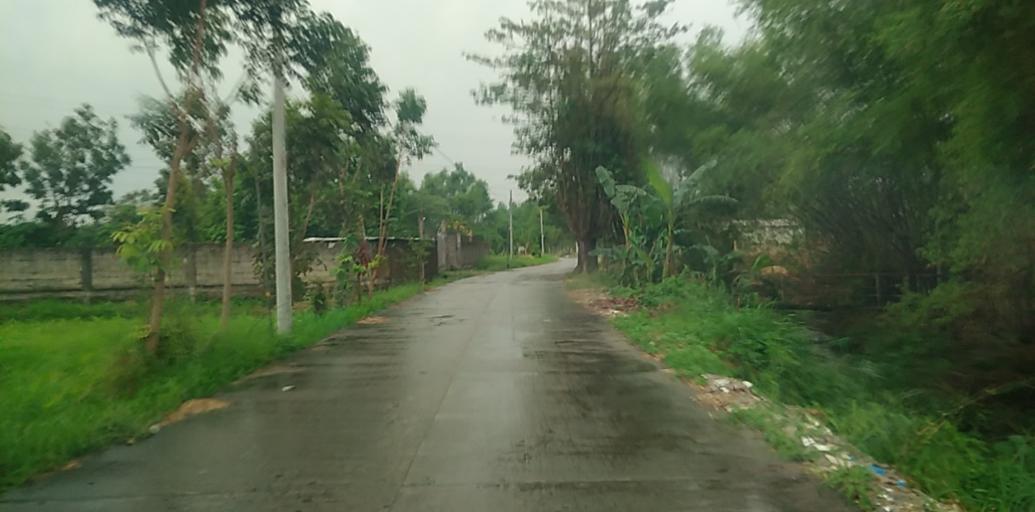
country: PH
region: Central Luzon
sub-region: Province of Pampanga
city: San Antonio
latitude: 15.1523
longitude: 120.6836
